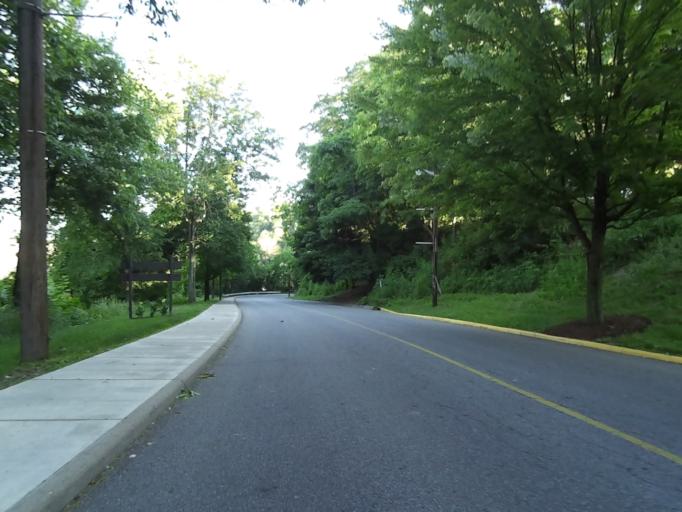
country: US
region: Ohio
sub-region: Jefferson County
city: Steubenville
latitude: 40.3759
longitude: -80.6198
